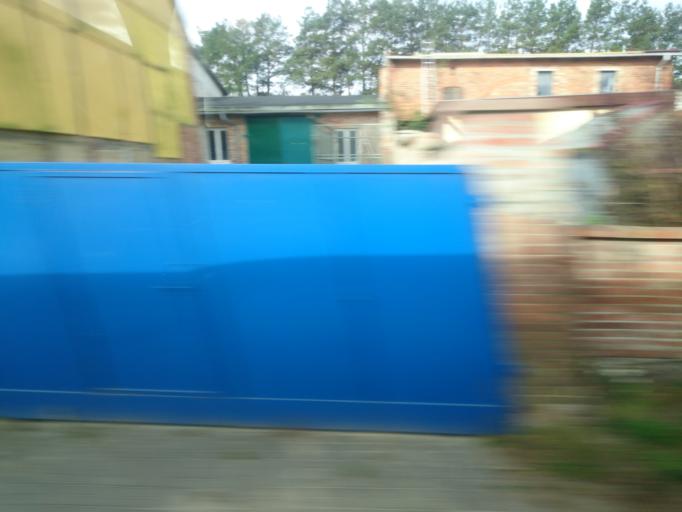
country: DE
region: Mecklenburg-Vorpommern
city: Jatznick
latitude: 53.5482
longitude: 13.9692
